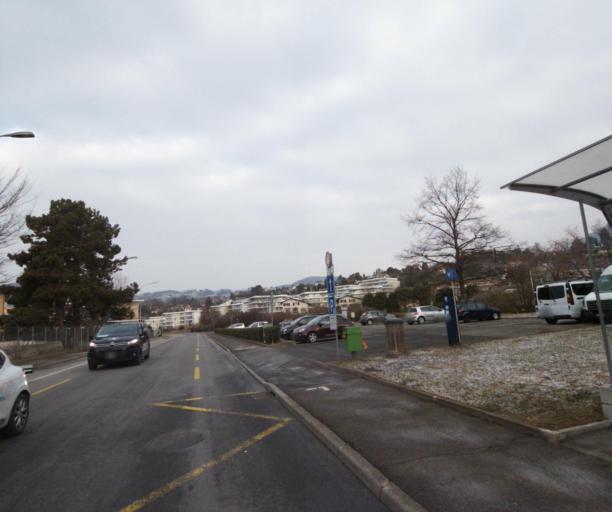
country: CH
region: Vaud
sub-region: Riviera-Pays-d'Enhaut District
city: La Tour-de-Peilz
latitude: 46.4552
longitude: 6.8670
